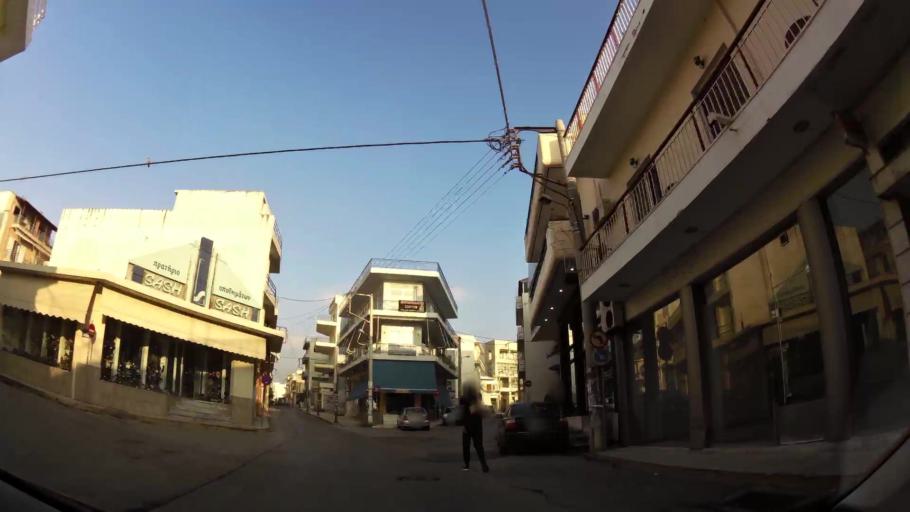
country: GR
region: Attica
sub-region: Nomarchia Anatolikis Attikis
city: Acharnes
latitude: 38.0824
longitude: 23.7337
